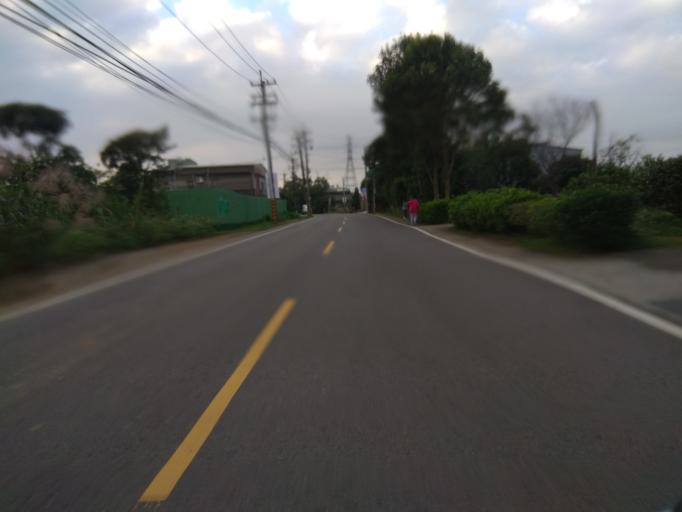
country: TW
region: Taiwan
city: Daxi
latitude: 24.8410
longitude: 121.2049
